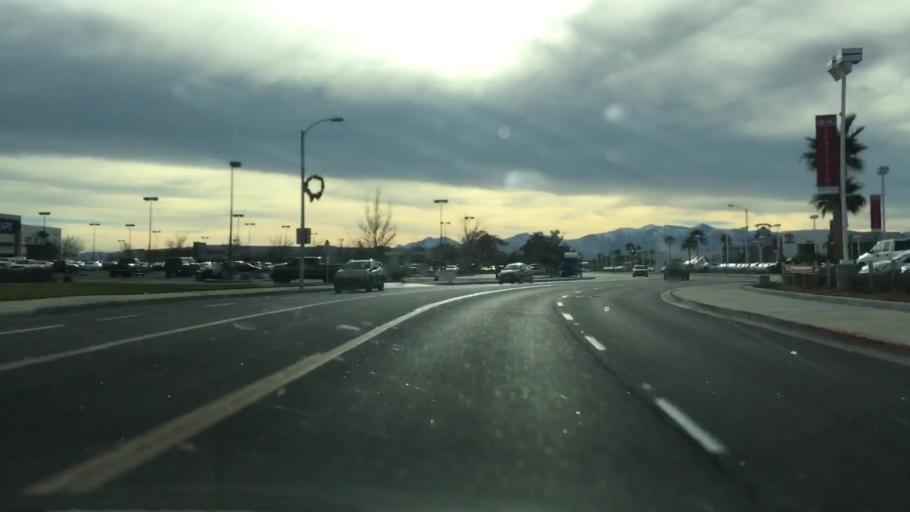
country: US
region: California
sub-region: San Bernardino County
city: Victorville
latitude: 34.5184
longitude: -117.3163
